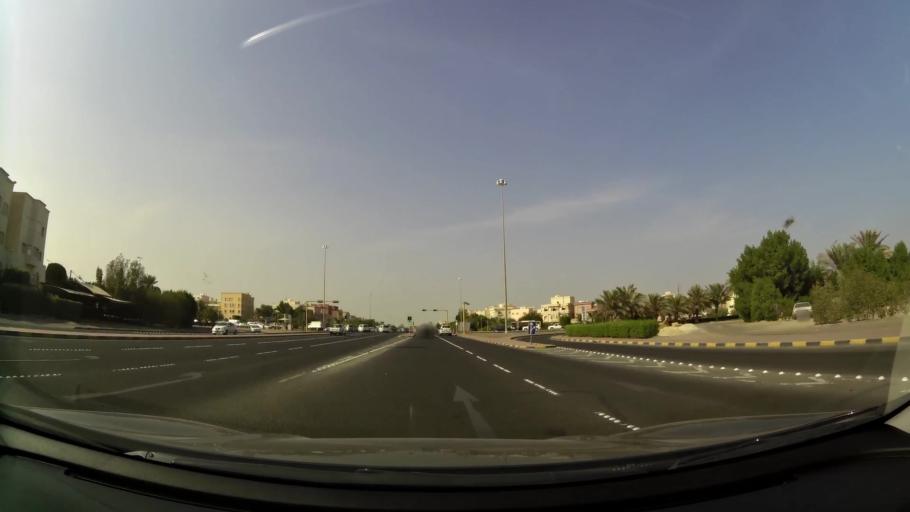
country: KW
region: Mubarak al Kabir
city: Mubarak al Kabir
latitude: 29.1793
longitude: 48.0832
